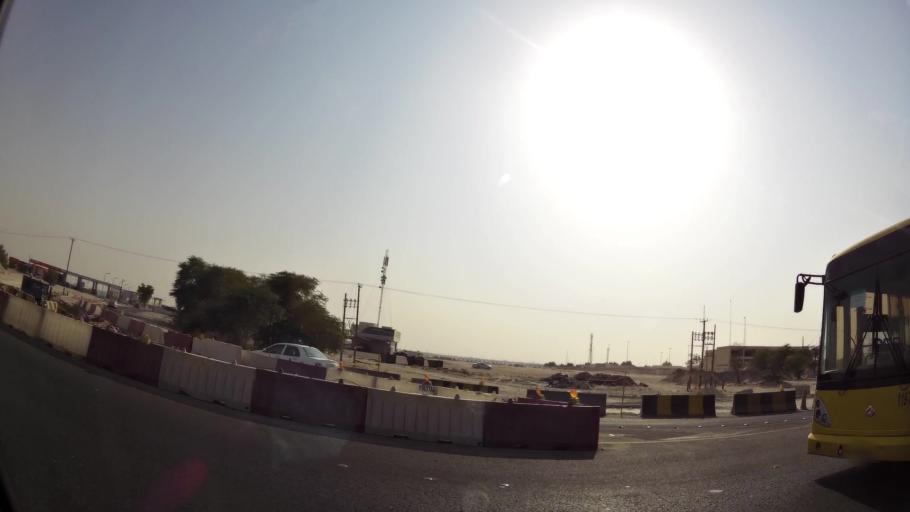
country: KW
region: Muhafazat al Jahra'
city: Al Jahra'
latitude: 29.3371
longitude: 47.7210
